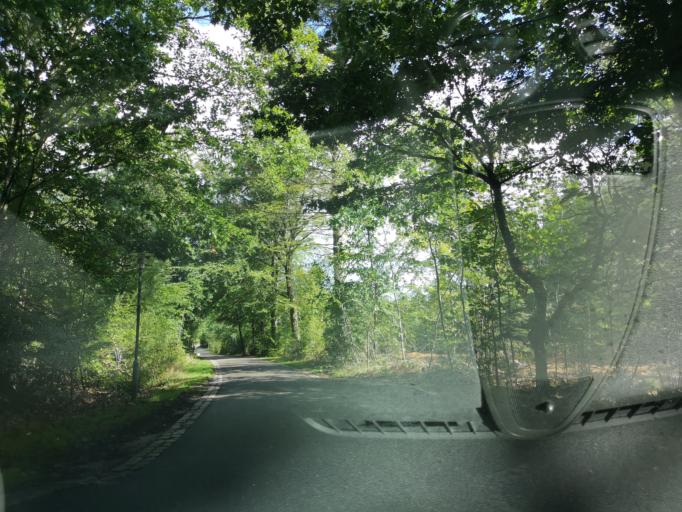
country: DK
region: Central Jutland
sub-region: Holstebro Kommune
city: Holstebro
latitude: 56.3375
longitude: 8.6319
